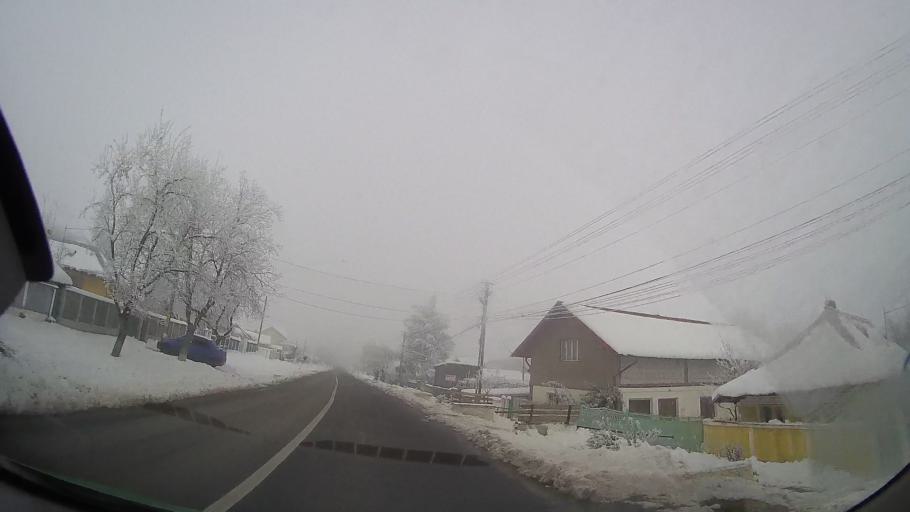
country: RO
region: Iasi
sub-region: Comuna Mircesti
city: Mircesti
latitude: 47.0958
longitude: 26.8196
